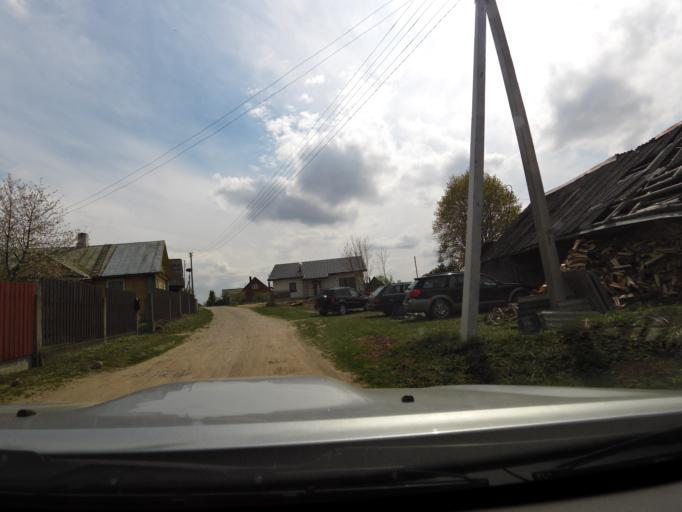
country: LT
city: Salcininkai
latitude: 54.4197
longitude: 25.3198
